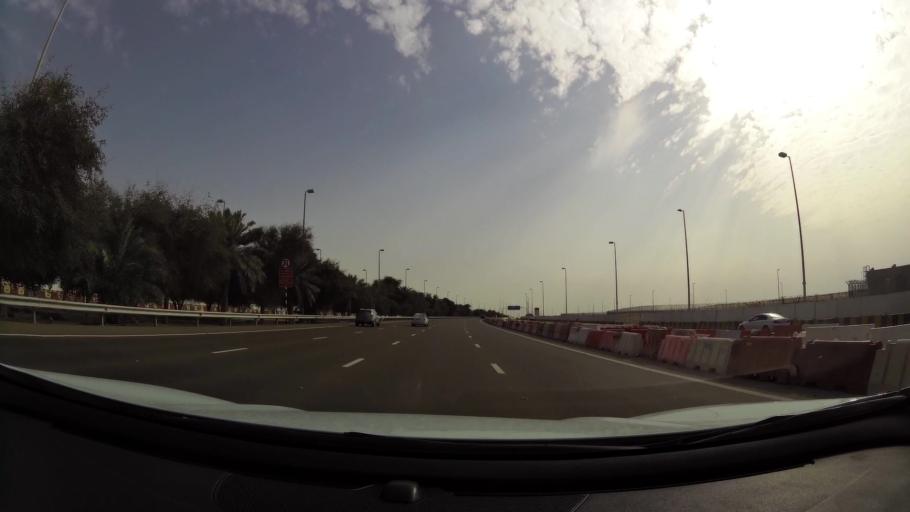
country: AE
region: Abu Dhabi
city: Abu Dhabi
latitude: 24.4196
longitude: 54.6769
